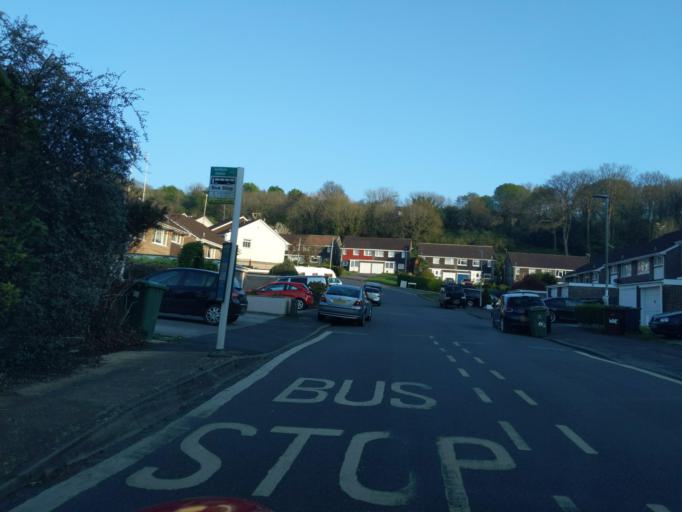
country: GB
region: England
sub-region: Plymouth
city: Plymstock
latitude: 50.3497
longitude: -4.0893
